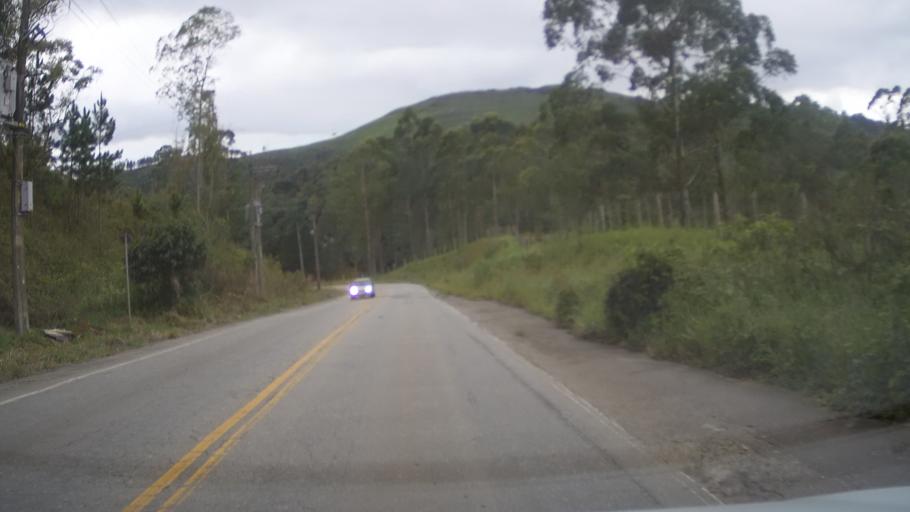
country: BR
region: Sao Paulo
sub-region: Aruja
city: Aruja
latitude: -23.3545
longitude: -46.4090
